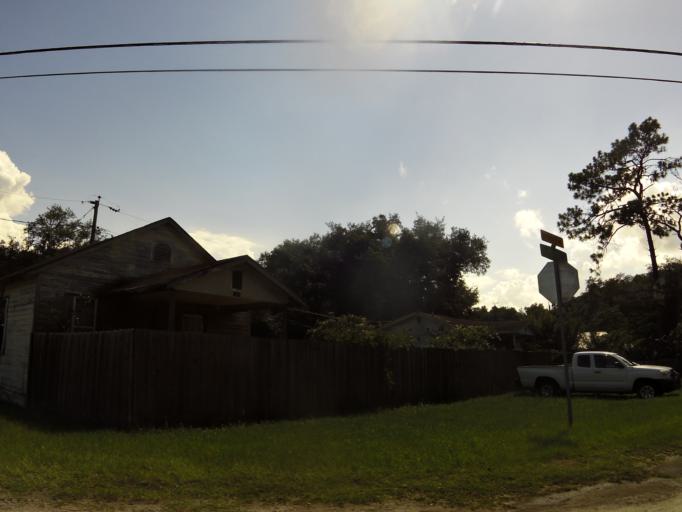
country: US
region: Florida
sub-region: Nassau County
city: Yulee
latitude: 30.5999
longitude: -81.5993
